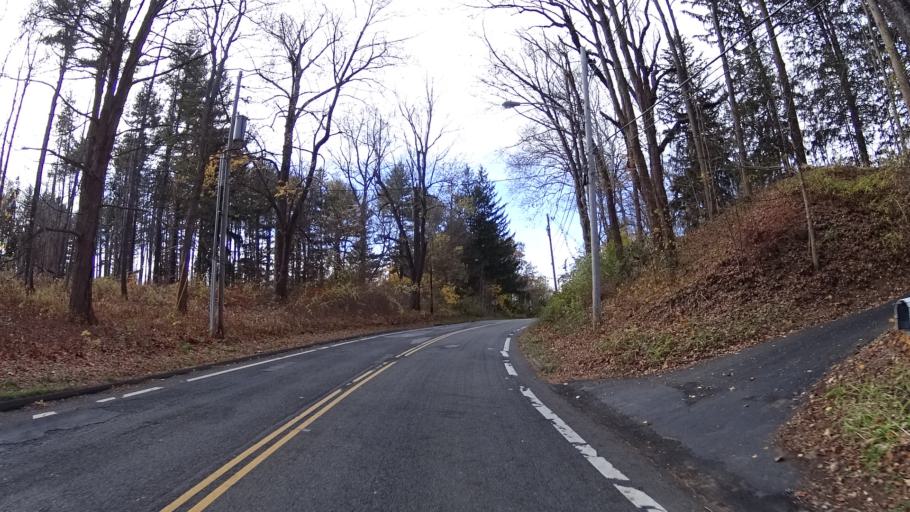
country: US
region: New Jersey
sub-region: Morris County
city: Morristown
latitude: 40.7913
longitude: -74.5249
